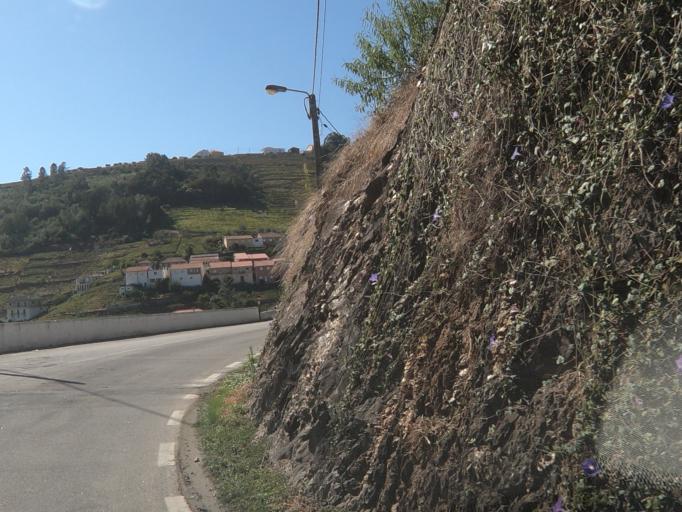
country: PT
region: Vila Real
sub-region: Santa Marta de Penaguiao
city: Santa Marta de Penaguiao
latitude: 41.2291
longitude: -7.7867
